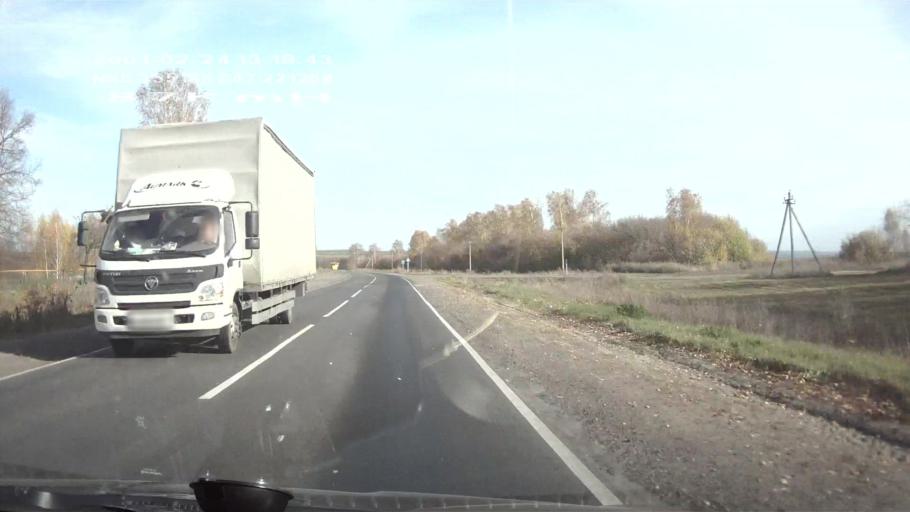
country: RU
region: Chuvashia
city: Ibresi
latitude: 55.3551
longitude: 47.2217
